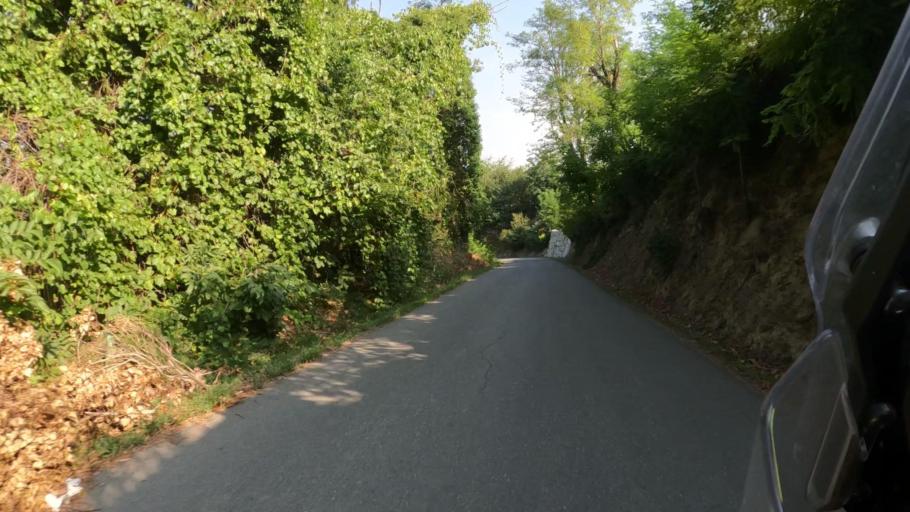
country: IT
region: Piedmont
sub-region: Provincia di Asti
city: Nizza Monferrato
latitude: 44.7613
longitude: 8.3783
